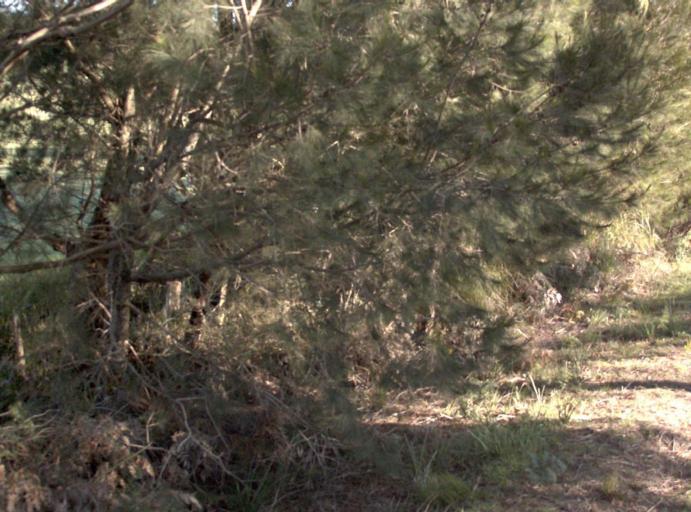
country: AU
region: Tasmania
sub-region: Dorset
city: Bridport
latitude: -41.1048
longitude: 147.1983
